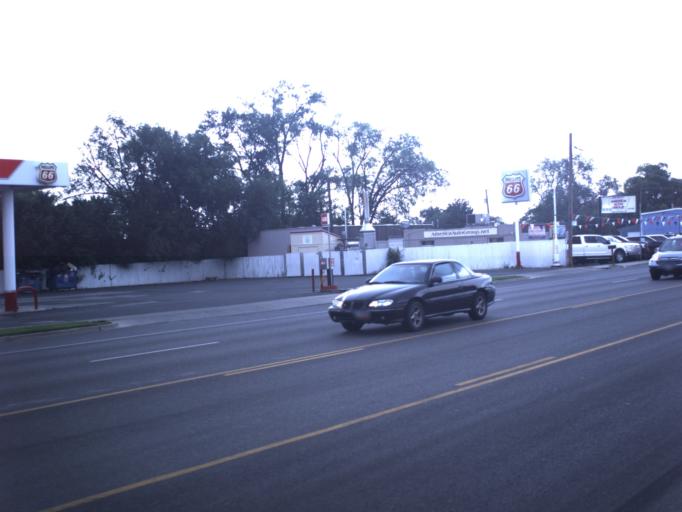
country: US
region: Utah
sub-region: Salt Lake County
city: Sandy City
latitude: 40.5992
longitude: -111.8907
